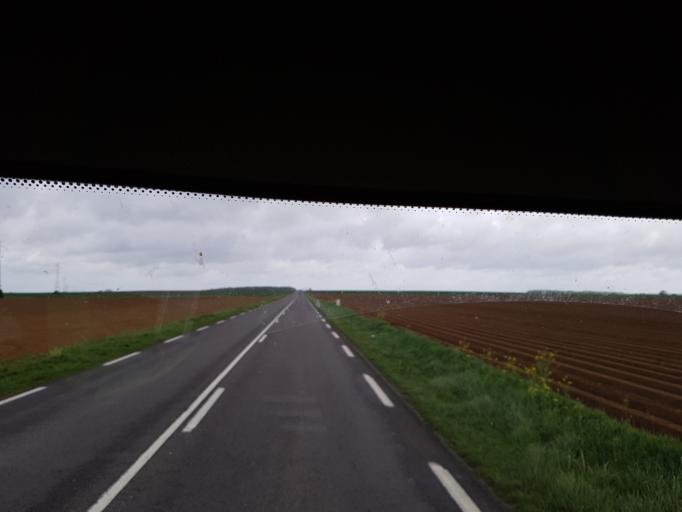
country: FR
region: Picardie
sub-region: Departement de l'Aisne
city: Crouy
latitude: 49.4205
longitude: 3.3465
